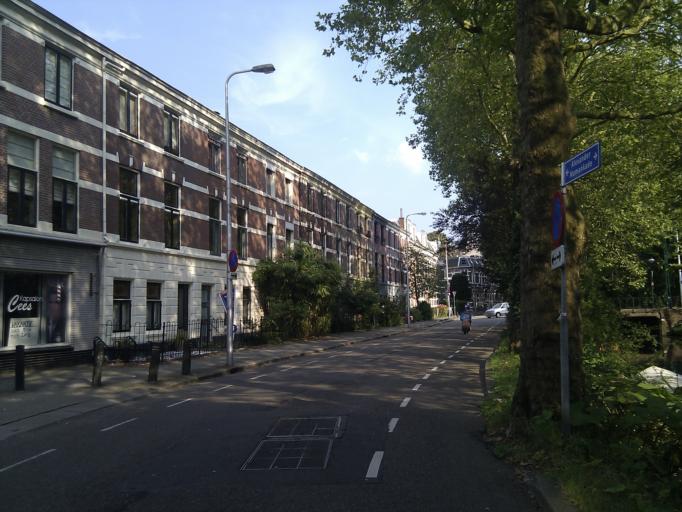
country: NL
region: Utrecht
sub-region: Gemeente Utrecht
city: Utrecht
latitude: 52.0998
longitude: 5.1361
